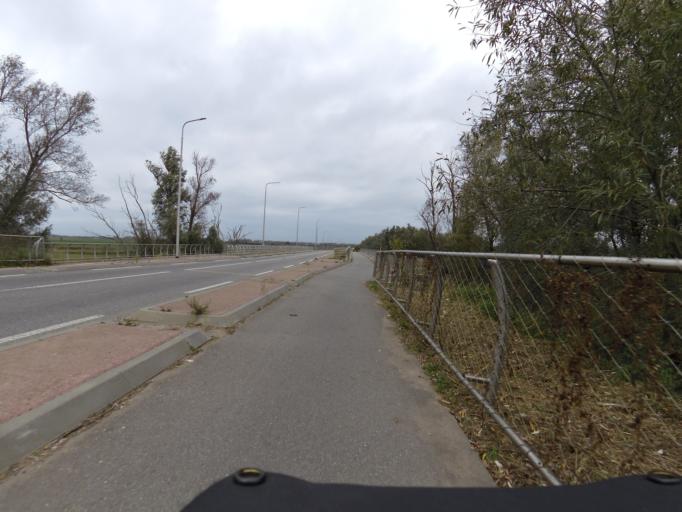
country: NL
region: Gelderland
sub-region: Gemeente Zevenaar
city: Zevenaar
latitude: 51.8920
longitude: 6.1027
